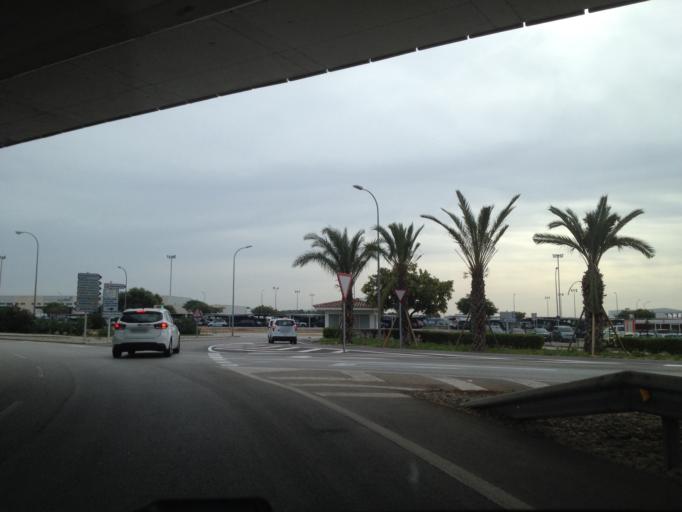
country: ES
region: Balearic Islands
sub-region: Illes Balears
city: s'Arenal
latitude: 39.5447
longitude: 2.7221
